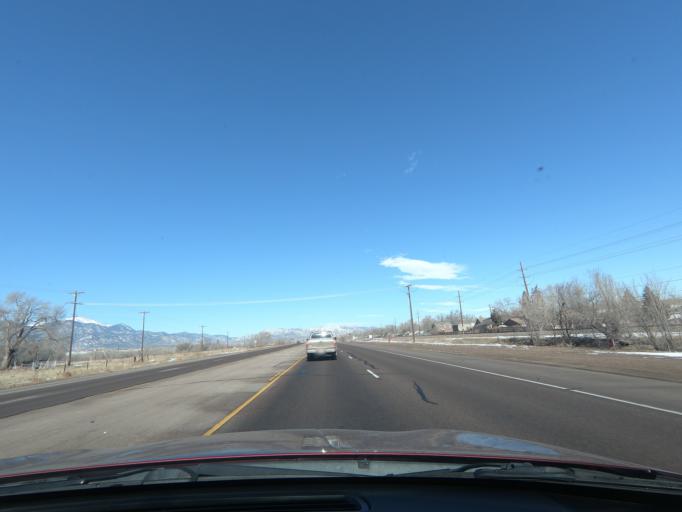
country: US
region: Colorado
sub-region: El Paso County
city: Stratmoor
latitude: 38.7601
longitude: -104.7522
